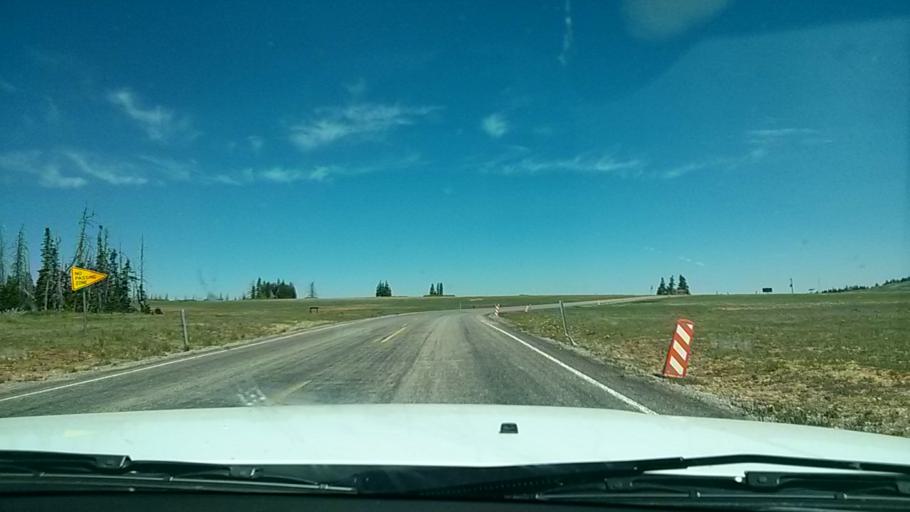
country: US
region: Utah
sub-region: Iron County
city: Parowan
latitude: 37.6593
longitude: -112.8361
